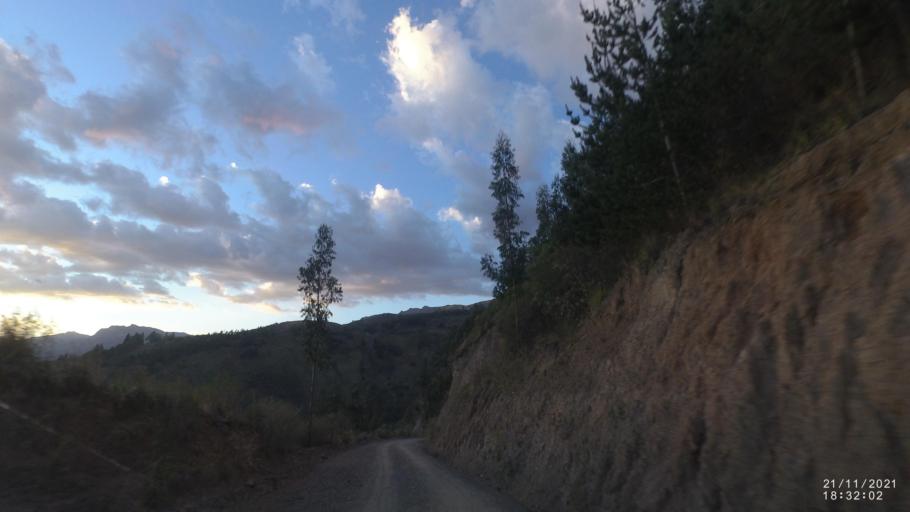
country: BO
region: Cochabamba
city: Cochabamba
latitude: -17.3103
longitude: -66.2173
